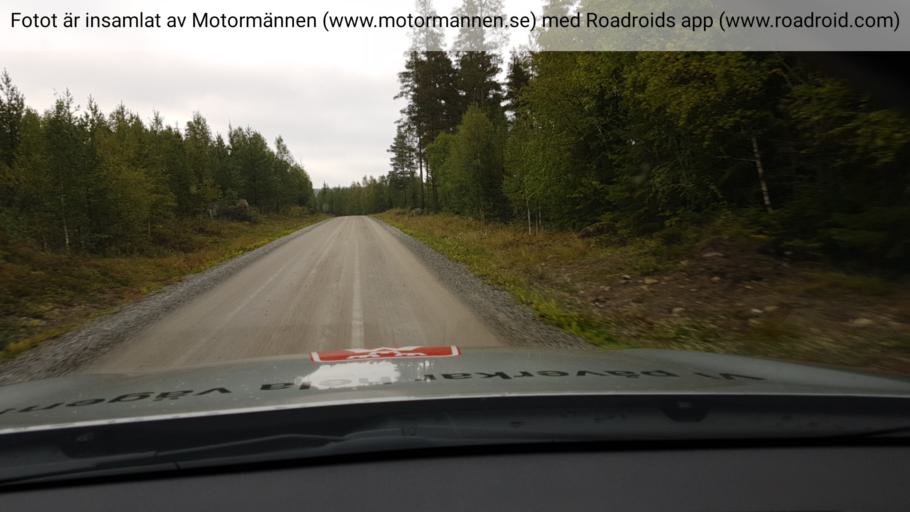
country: SE
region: Jaemtland
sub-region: Braecke Kommun
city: Braecke
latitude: 62.7383
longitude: 15.4909
